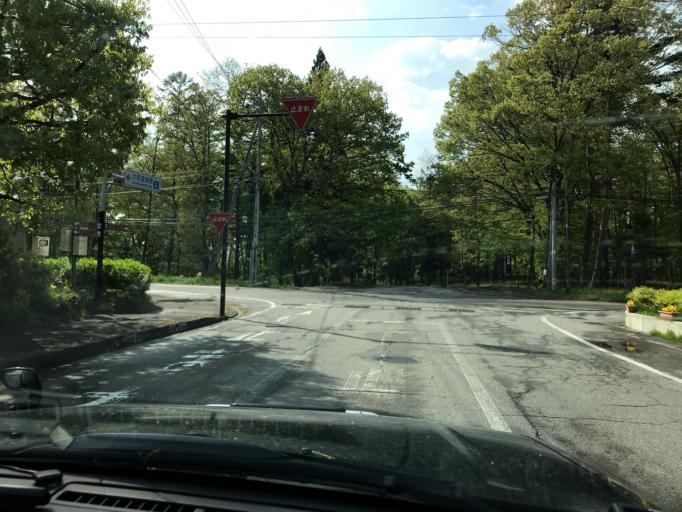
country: JP
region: Nagano
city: Omachi
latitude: 36.5269
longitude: 137.8116
